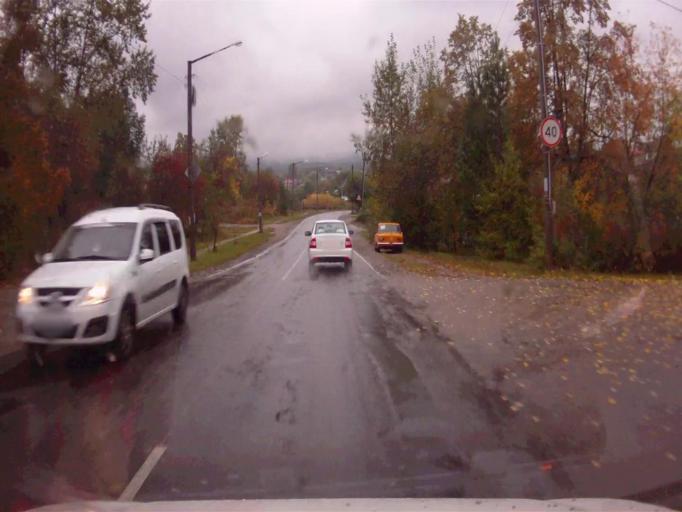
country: RU
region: Chelyabinsk
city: Kyshtym
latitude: 55.7227
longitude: 60.5291
